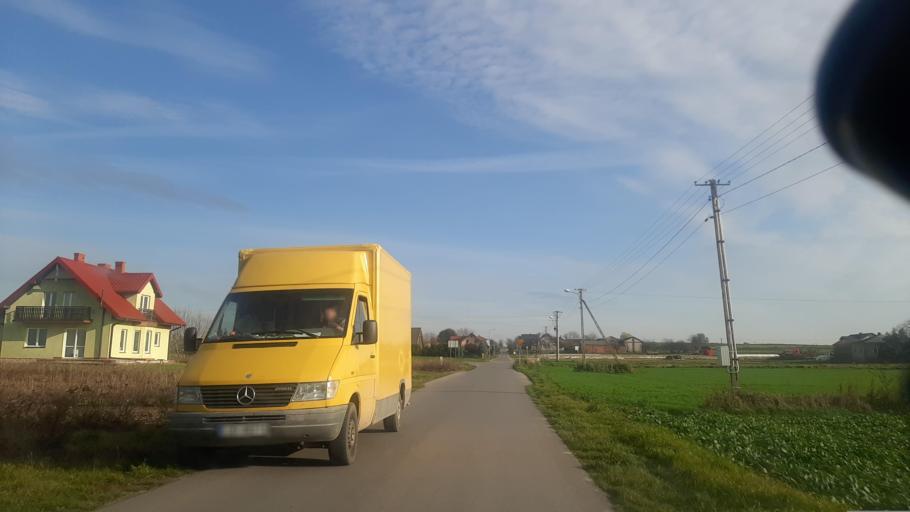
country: PL
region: Lublin Voivodeship
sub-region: Powiat lubelski
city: Garbow
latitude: 51.3901
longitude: 22.3286
